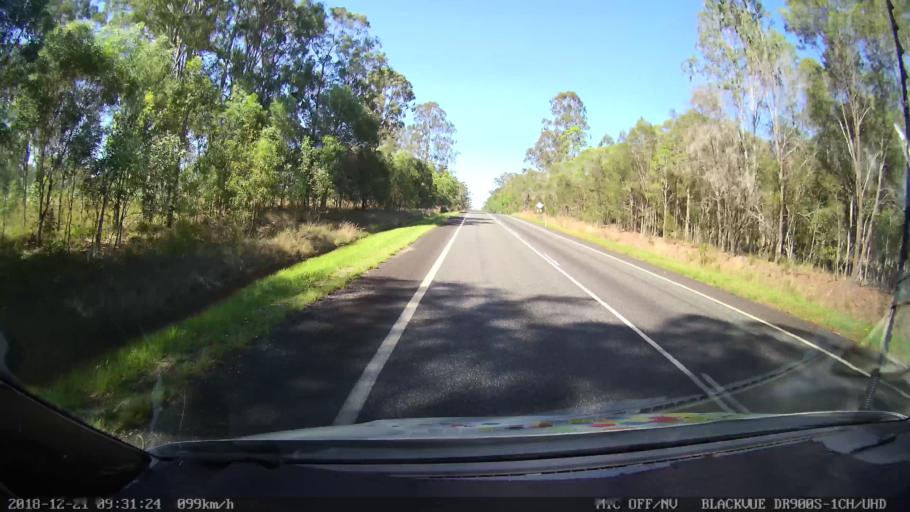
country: AU
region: New South Wales
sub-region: Clarence Valley
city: Maclean
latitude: -29.4596
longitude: 152.9892
